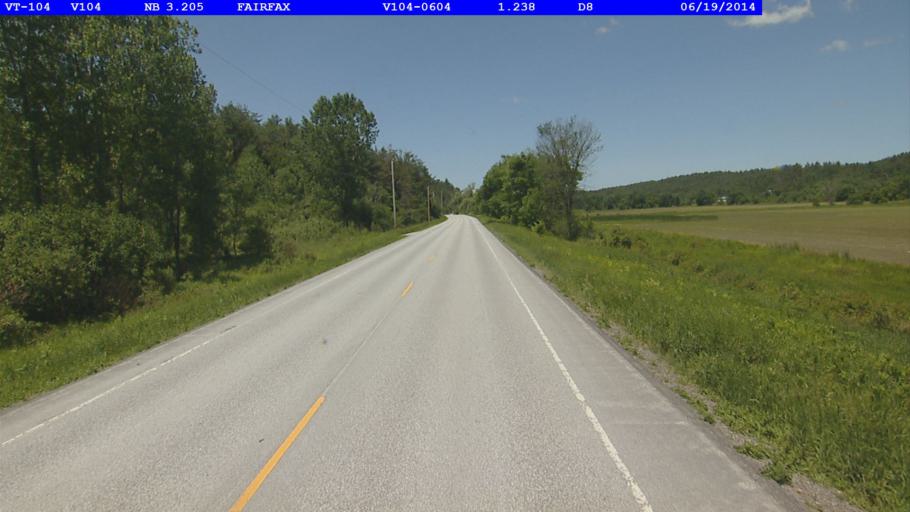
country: US
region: Vermont
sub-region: Chittenden County
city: Jericho
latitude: 44.6448
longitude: -72.9489
